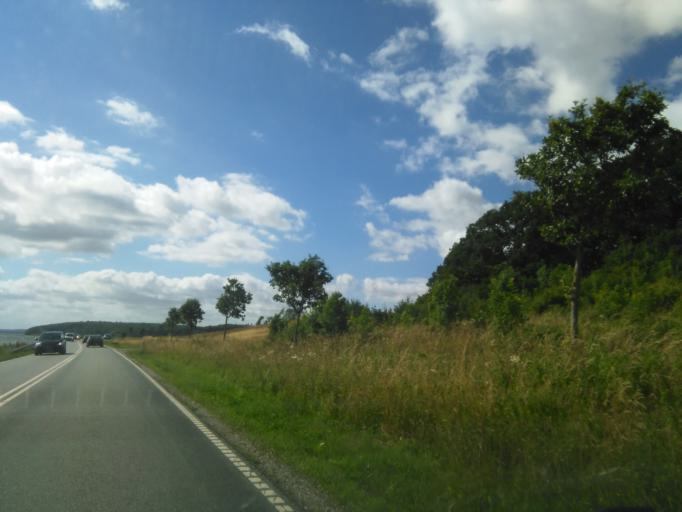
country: DK
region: Central Jutland
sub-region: Syddjurs Kommune
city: Ronde
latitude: 56.2782
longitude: 10.4928
